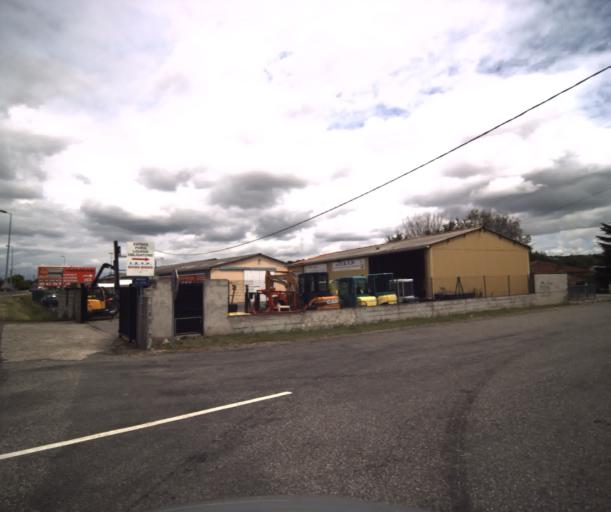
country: FR
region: Midi-Pyrenees
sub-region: Departement de la Haute-Garonne
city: Lacroix-Falgarde
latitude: 43.4825
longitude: 1.4003
